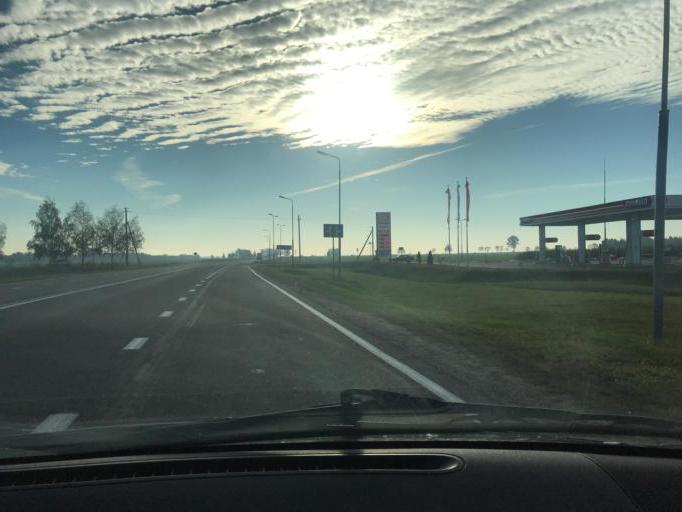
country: BY
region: Brest
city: Drahichyn
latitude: 52.2083
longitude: 25.2174
